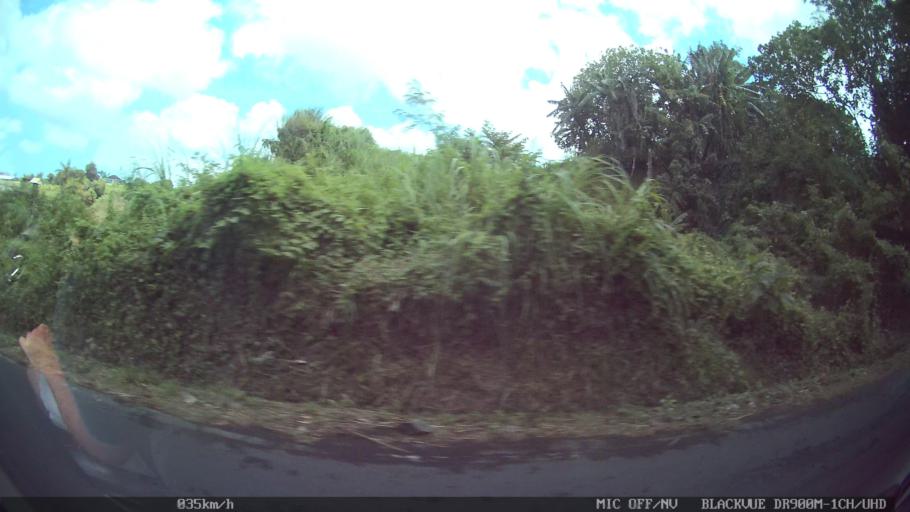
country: ID
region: Bali
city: Banjar Desa
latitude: -8.5857
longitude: 115.2877
